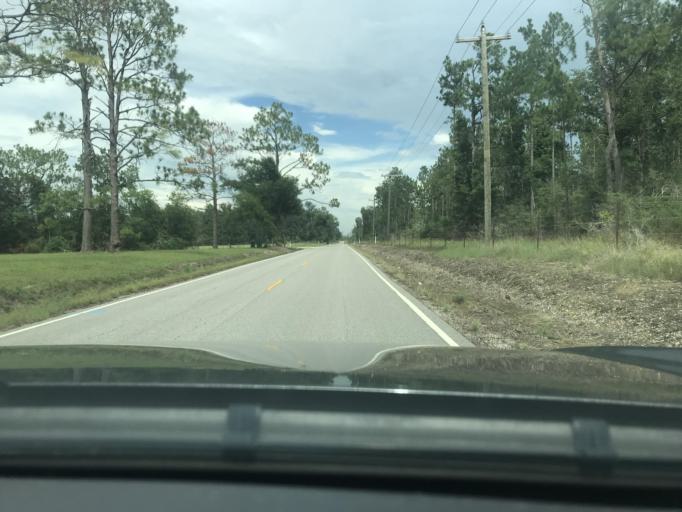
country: US
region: Louisiana
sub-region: Calcasieu Parish
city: Moss Bluff
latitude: 30.3885
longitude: -93.2440
